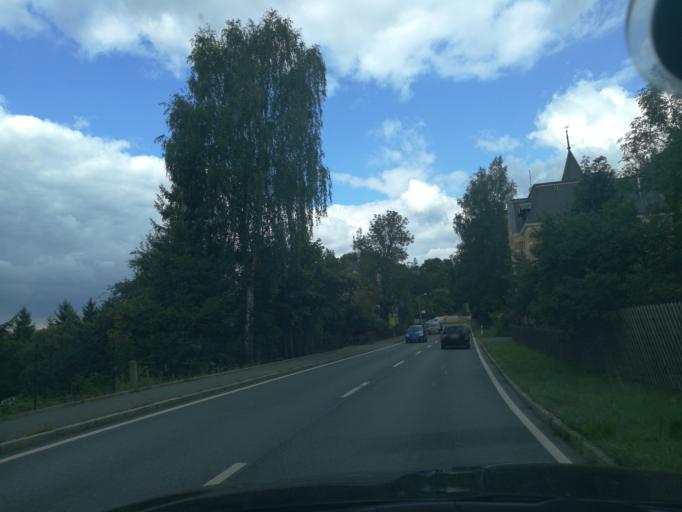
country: DE
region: Saxony
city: Oelsnitz
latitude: 50.4088
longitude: 12.1799
